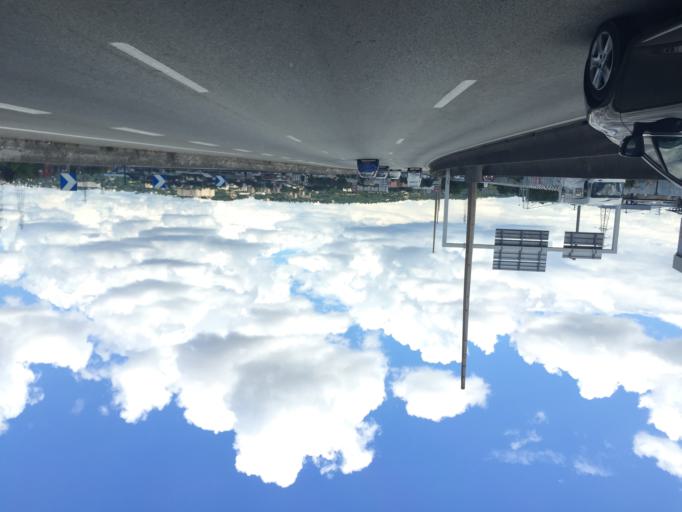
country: FR
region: Rhone-Alpes
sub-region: Departement du Rhone
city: Pierre-Benite
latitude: 45.7098
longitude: 4.8285
